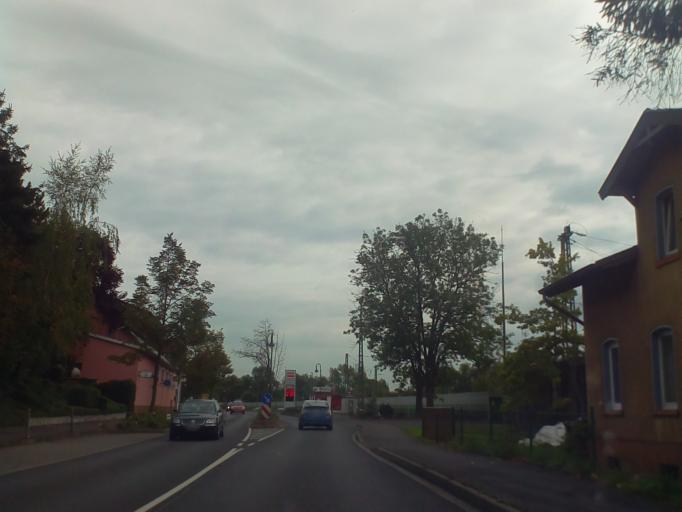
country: DE
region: Hesse
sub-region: Regierungsbezirk Kassel
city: Burghaun
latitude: 50.7035
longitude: 9.7239
